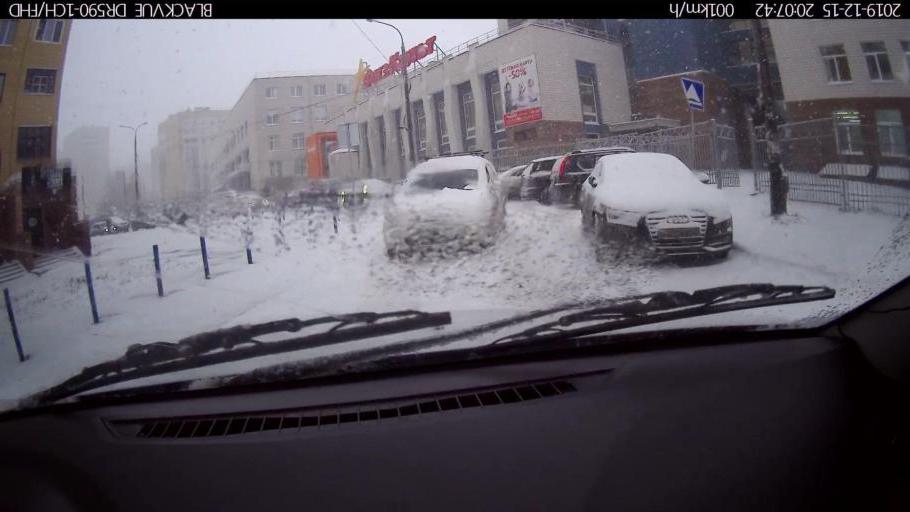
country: RU
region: Nizjnij Novgorod
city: Afonino
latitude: 56.3026
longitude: 44.0743
